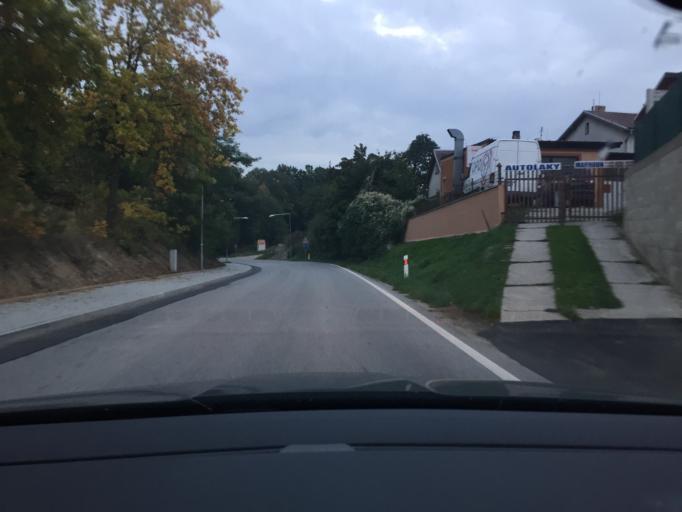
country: CZ
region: Jihocesky
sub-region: Okres Ceske Budejovice
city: Hluboka nad Vltavou
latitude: 49.0555
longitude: 14.4581
